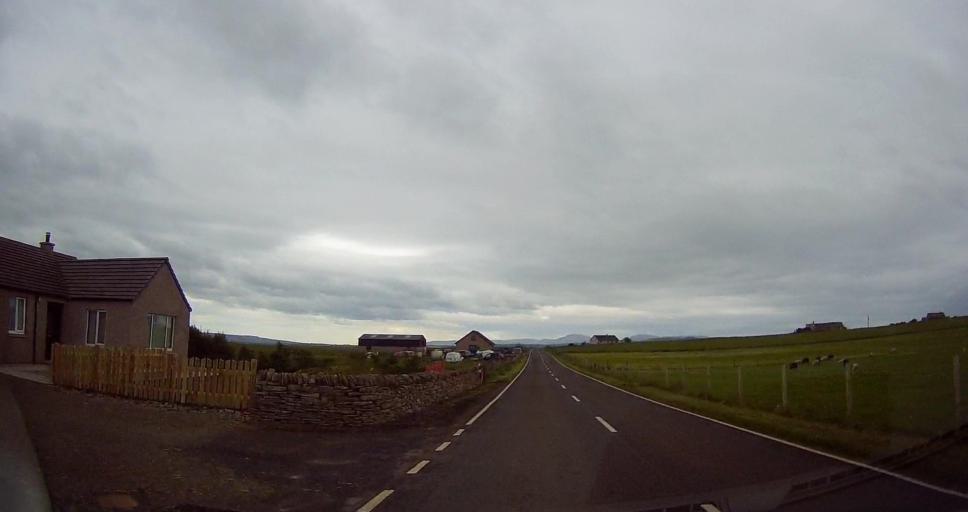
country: GB
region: Scotland
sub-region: Orkney Islands
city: Stromness
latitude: 59.0786
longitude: -3.2774
